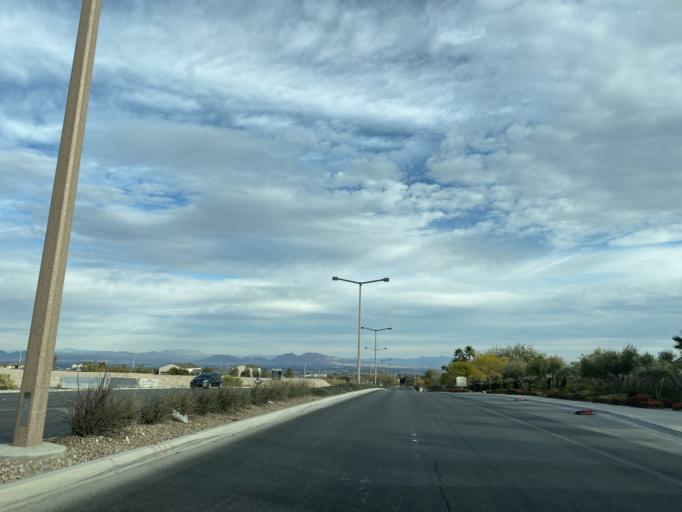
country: US
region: Nevada
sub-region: Clark County
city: Summerlin South
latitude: 36.1814
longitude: -115.3528
